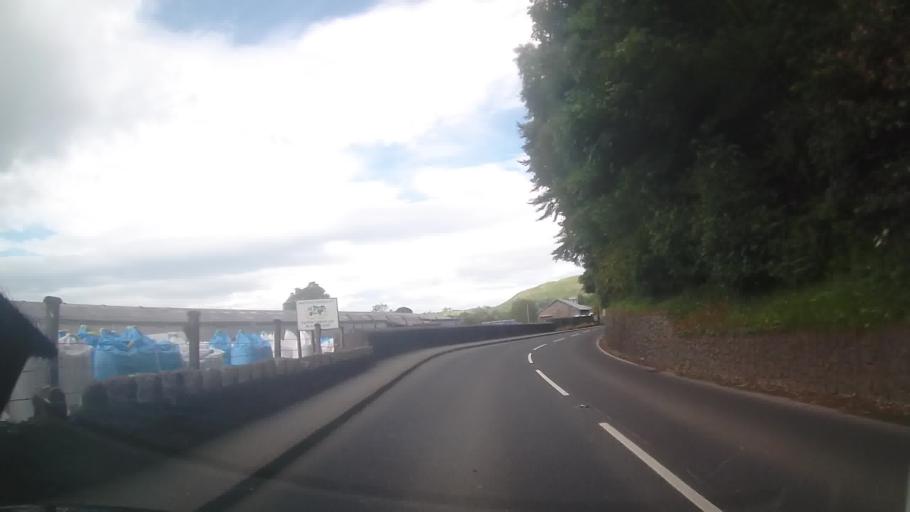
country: GB
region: Wales
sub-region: Denbighshire
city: Corwen
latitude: 52.9795
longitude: -3.3838
